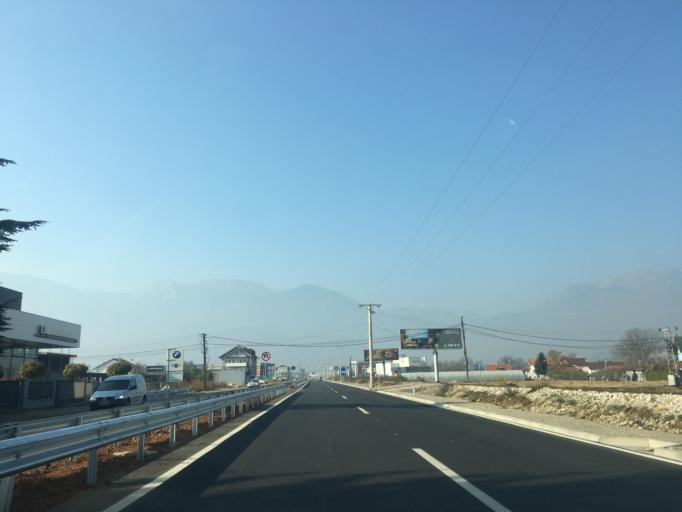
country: XK
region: Pec
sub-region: Komuna e Pejes
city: Peje
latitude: 42.6577
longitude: 20.3352
